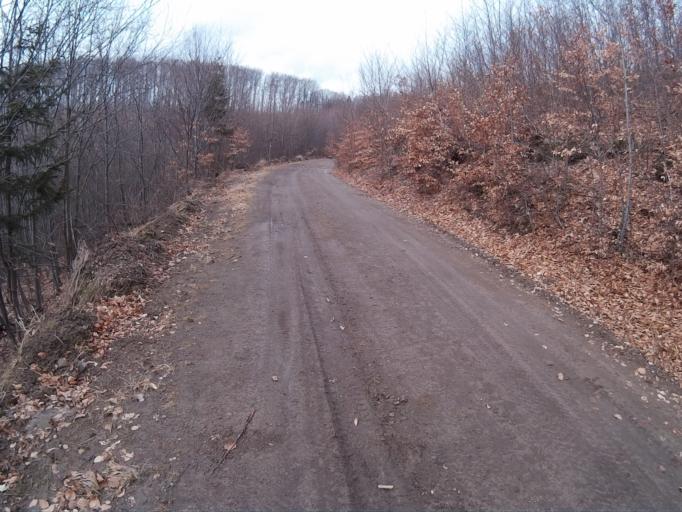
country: HU
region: Borsod-Abauj-Zemplen
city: Tolcsva
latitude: 48.4031
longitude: 21.4235
